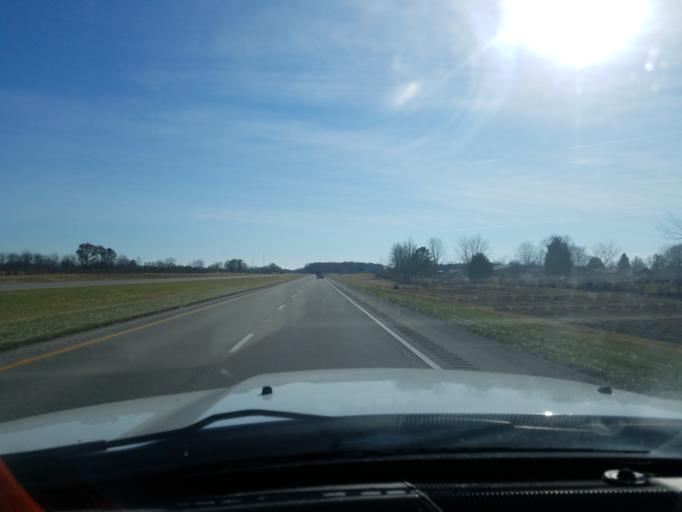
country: US
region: Ohio
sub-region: Adams County
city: Winchester
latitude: 38.9785
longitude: -83.7472
